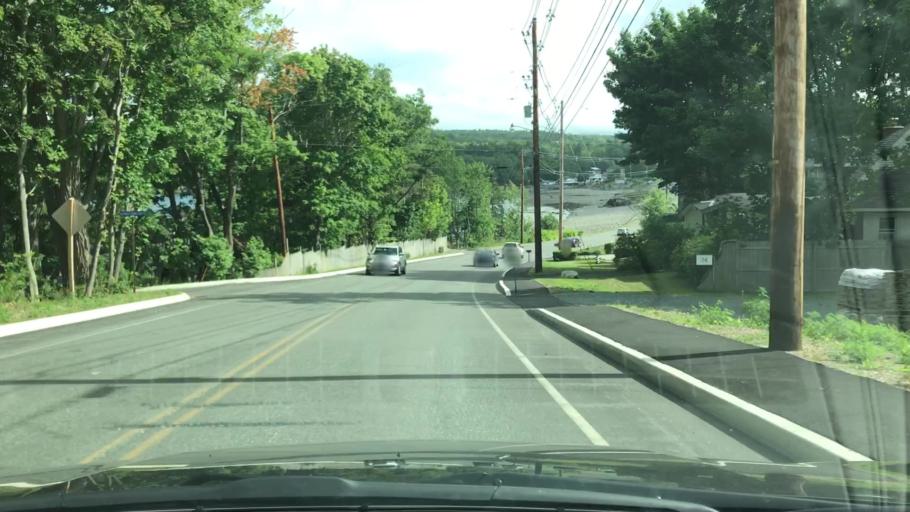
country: US
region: Maine
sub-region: Hancock County
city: Bar Harbor
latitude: 44.4195
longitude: -68.2502
